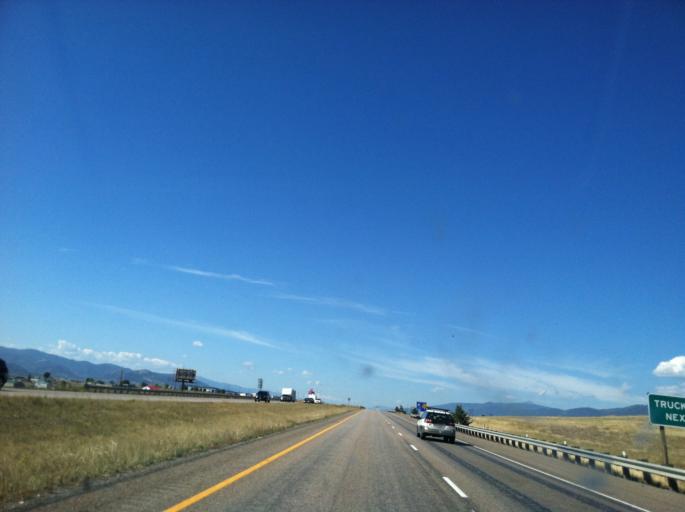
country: US
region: Montana
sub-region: Missoula County
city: Orchard Homes
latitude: 46.9432
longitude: -114.1169
